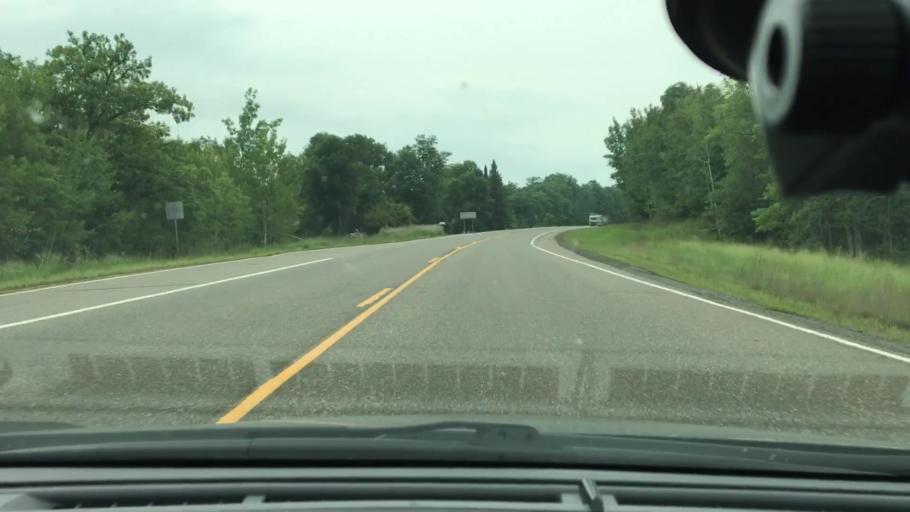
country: US
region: Minnesota
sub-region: Crow Wing County
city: Crosby
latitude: 46.5379
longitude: -93.9498
